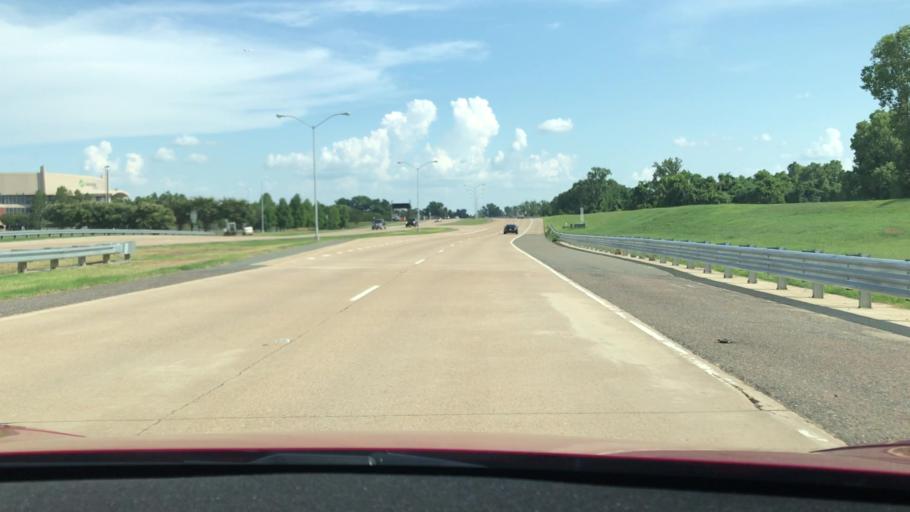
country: US
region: Louisiana
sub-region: Bossier Parish
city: Bossier City
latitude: 32.4689
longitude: -93.6775
